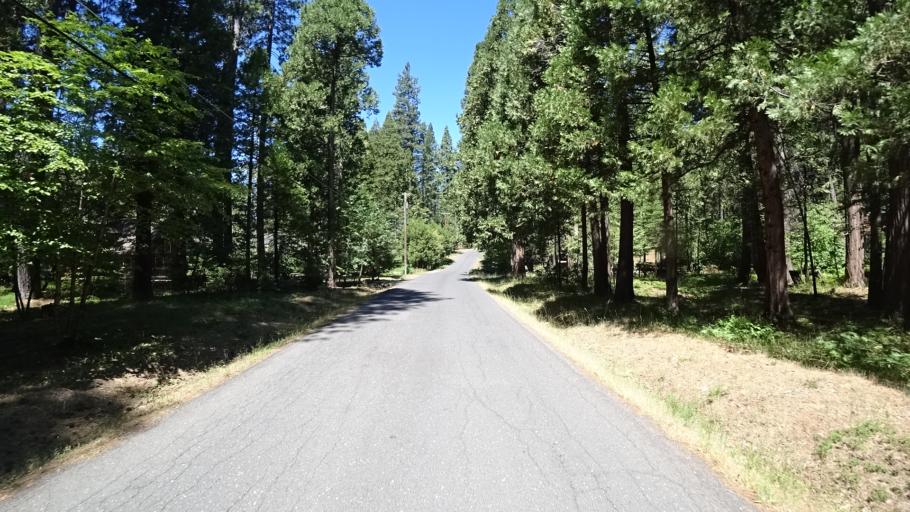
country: US
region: California
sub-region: Calaveras County
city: Arnold
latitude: 38.2347
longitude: -120.3362
